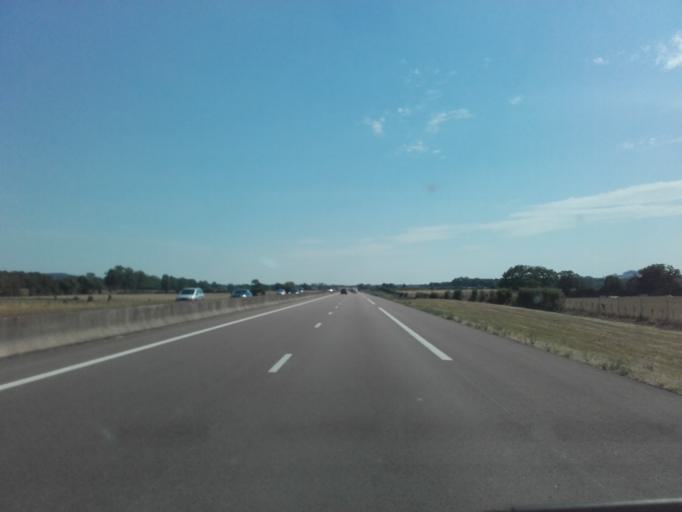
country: FR
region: Bourgogne
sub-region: Departement de la Cote-d'Or
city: Pouilly-en-Auxois
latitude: 47.2865
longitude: 4.5078
